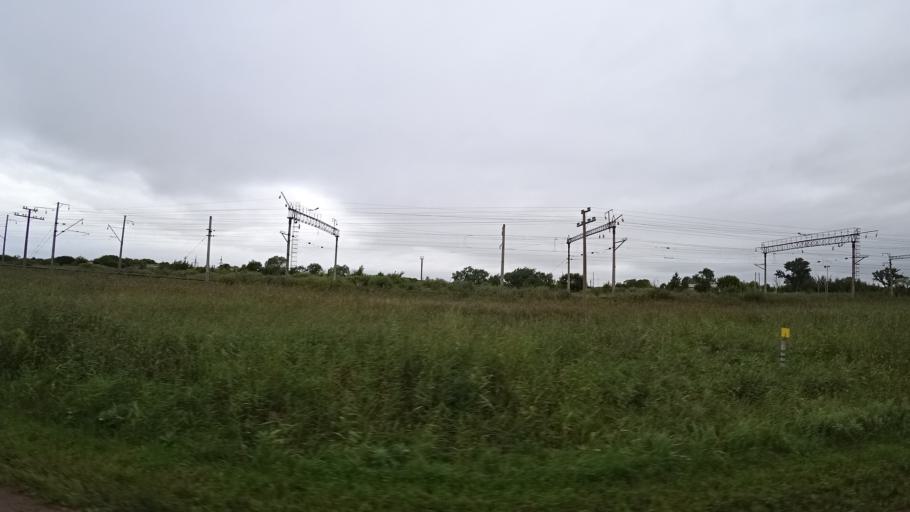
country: RU
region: Primorskiy
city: Chernigovka
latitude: 44.3342
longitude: 132.5258
